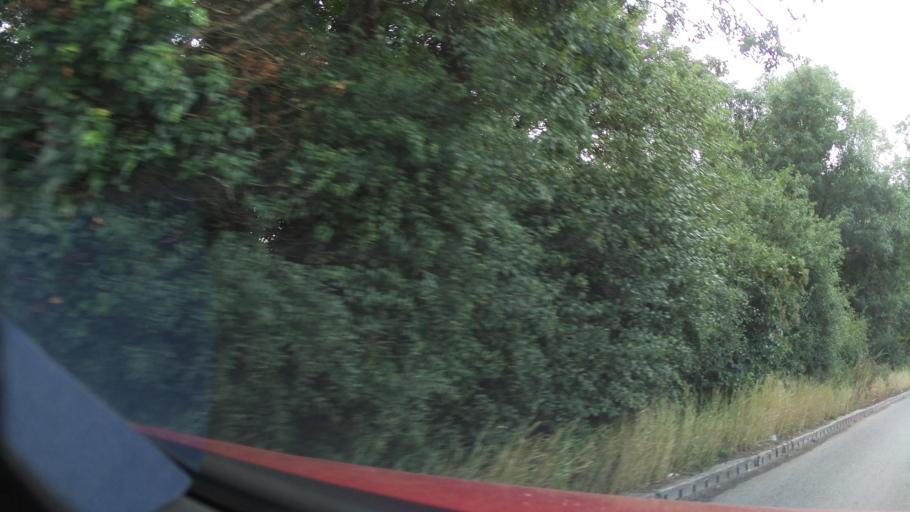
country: GB
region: England
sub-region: Warwickshire
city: Rugby
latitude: 52.3827
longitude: -1.2683
